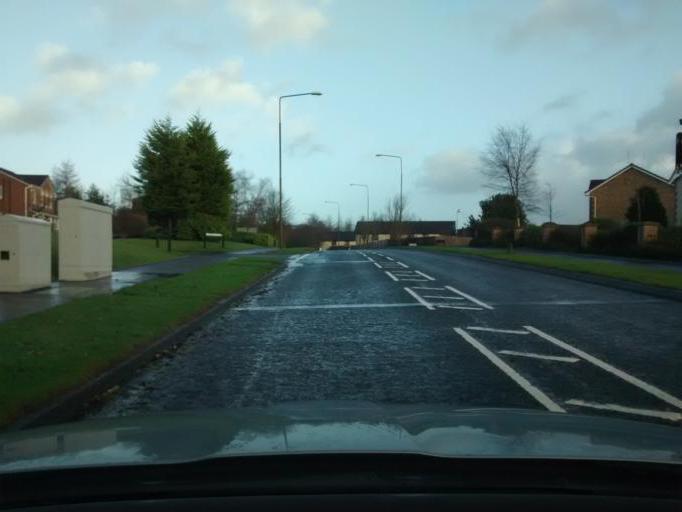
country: GB
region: Scotland
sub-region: West Lothian
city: Livingston
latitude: 55.8907
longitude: -3.5449
